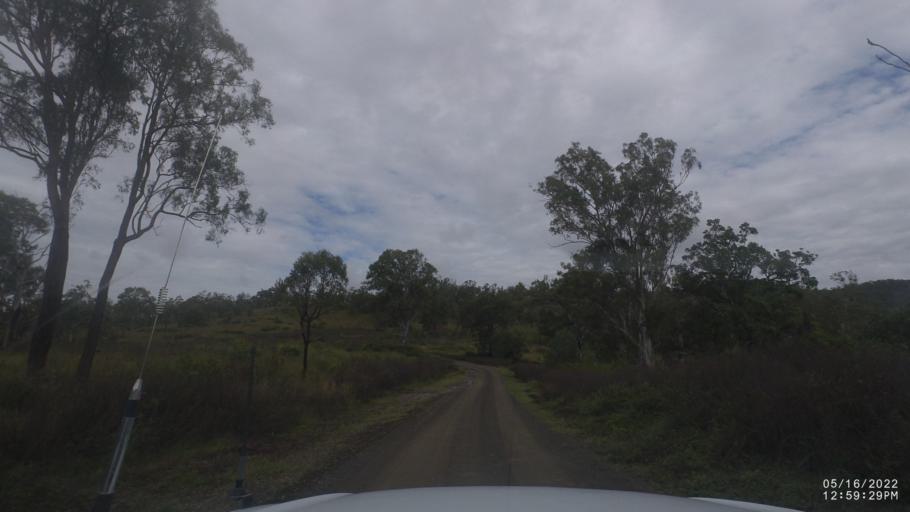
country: AU
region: Queensland
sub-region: Logan
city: Cedar Vale
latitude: -27.8673
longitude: 152.8400
